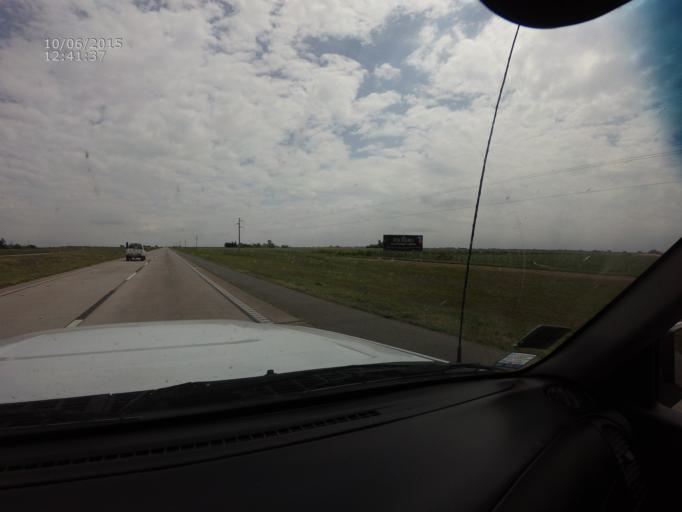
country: AR
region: Santa Fe
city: Canada de Gomez
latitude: -32.8605
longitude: -61.3087
